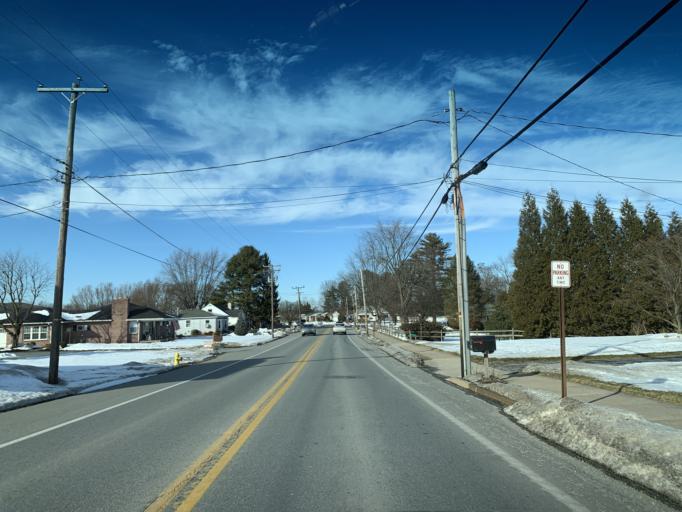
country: US
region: Pennsylvania
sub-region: York County
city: Dillsburg
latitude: 40.0992
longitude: -77.0309
